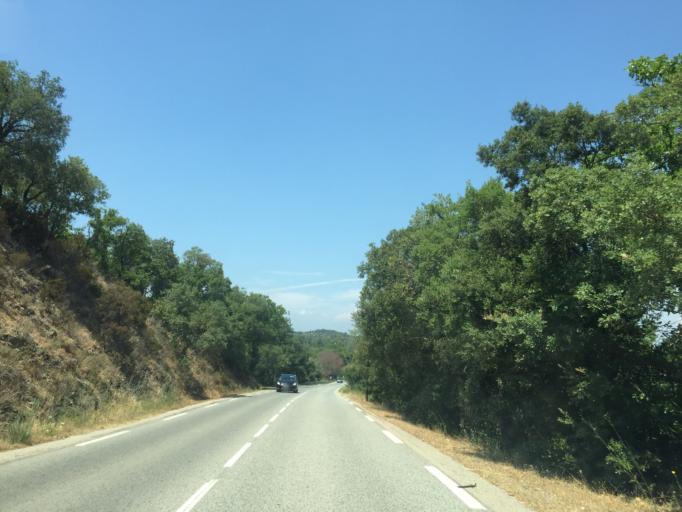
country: FR
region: Provence-Alpes-Cote d'Azur
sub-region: Departement du Var
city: Puget-sur-Argens
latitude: 43.3945
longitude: 6.6752
